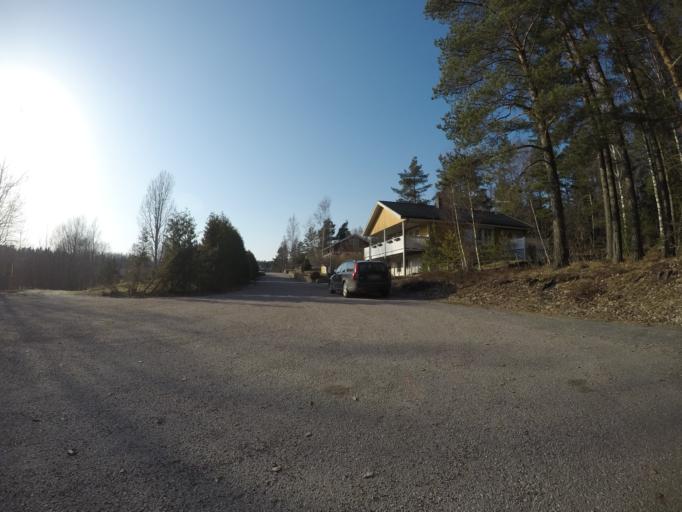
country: SE
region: Vaestmanland
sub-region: Kungsors Kommun
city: Kungsoer
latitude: 59.4045
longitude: 16.1139
